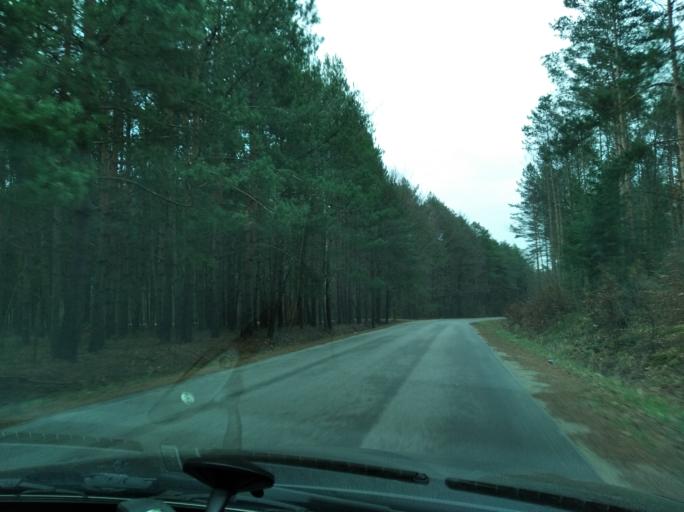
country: PL
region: Subcarpathian Voivodeship
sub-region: Powiat lancucki
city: Czarna
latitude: 50.1613
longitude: 22.1830
